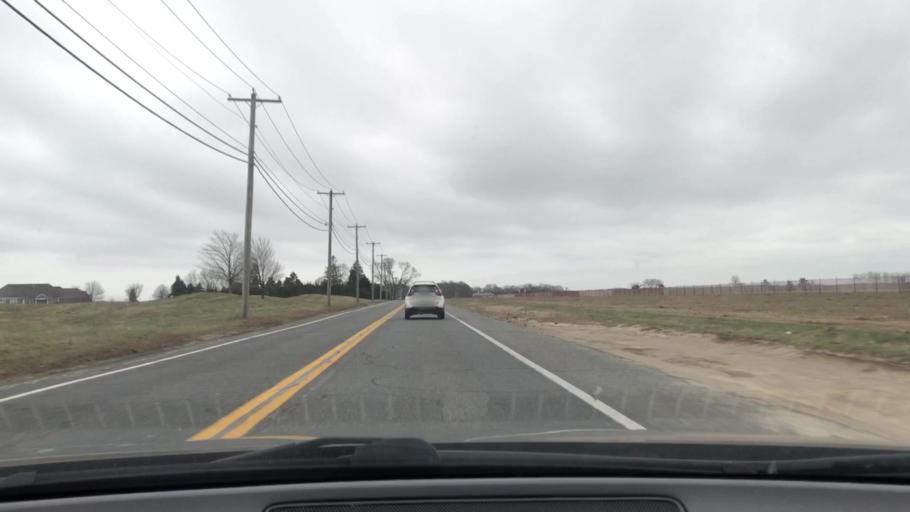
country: US
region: New York
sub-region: Suffolk County
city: Northville
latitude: 40.9663
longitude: -72.6490
